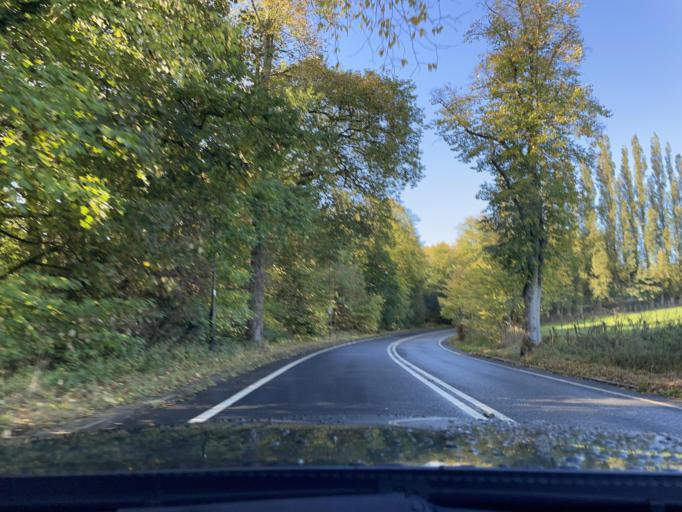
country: GB
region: England
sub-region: Sheffield
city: Oughtibridge
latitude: 53.3826
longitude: -1.5517
